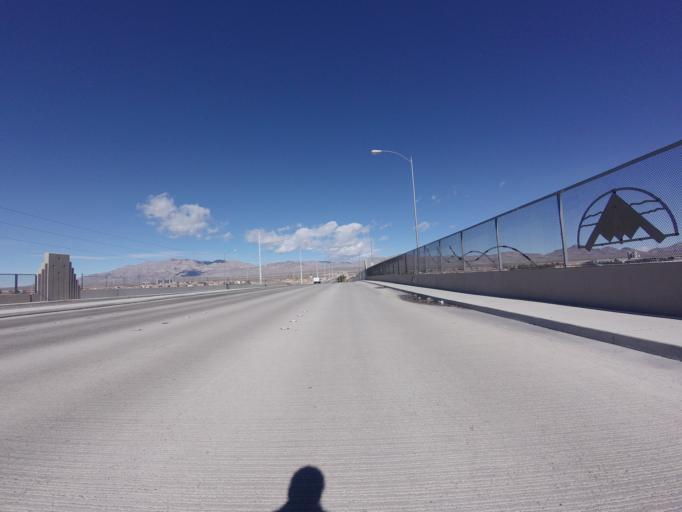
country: US
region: Nevada
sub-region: Clark County
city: Nellis Air Force Base
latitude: 36.2663
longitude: -115.0797
